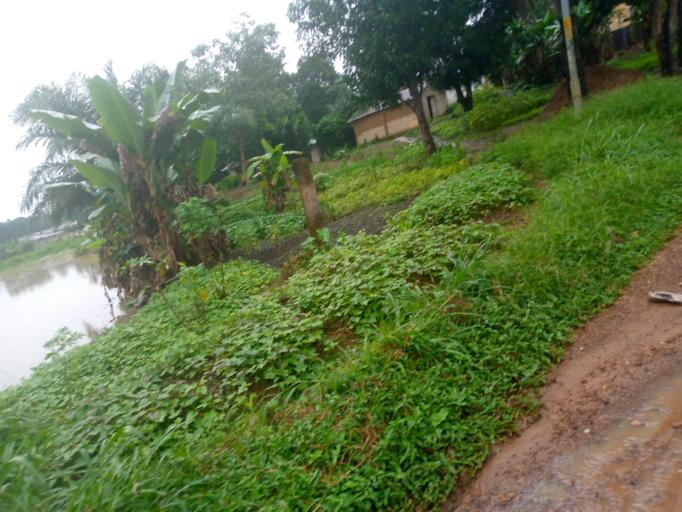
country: SL
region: Eastern Province
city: Kenema
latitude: 7.8794
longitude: -11.1773
